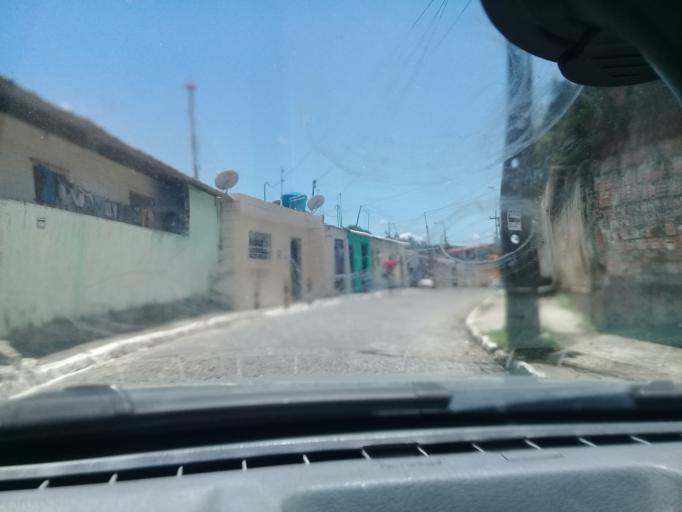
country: BR
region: Pernambuco
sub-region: Jaboatao Dos Guararapes
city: Jaboatao dos Guararapes
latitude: -8.1261
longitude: -34.9533
